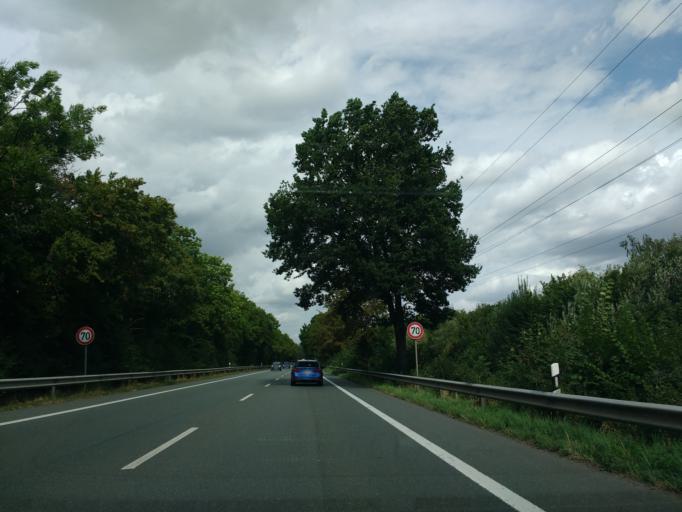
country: DE
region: North Rhine-Westphalia
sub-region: Regierungsbezirk Detmold
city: Petershagen
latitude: 52.3640
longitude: 8.9837
